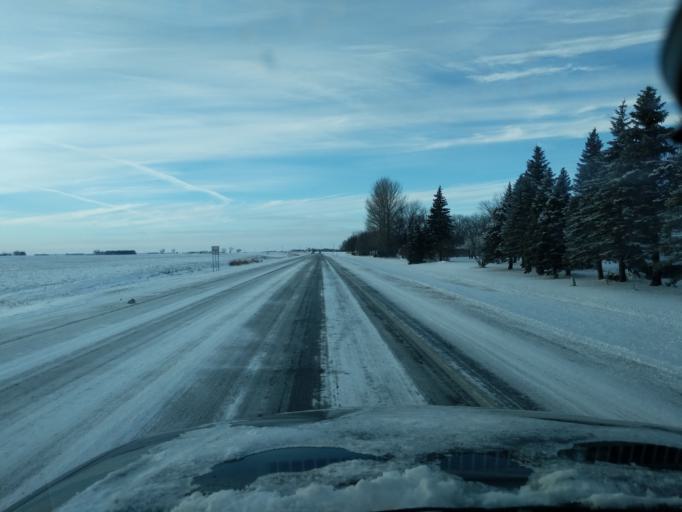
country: US
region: Minnesota
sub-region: Renville County
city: Hector
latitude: 44.7438
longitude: -94.7262
